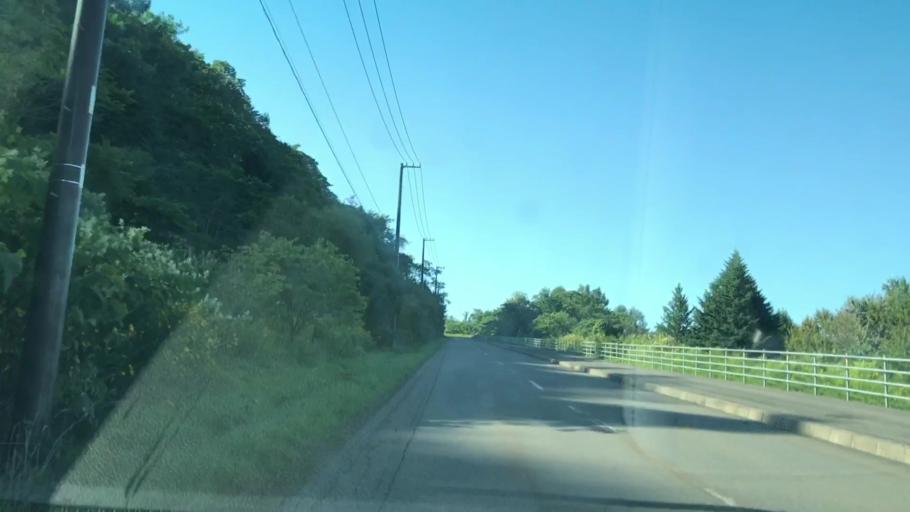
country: JP
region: Hokkaido
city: Date
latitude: 42.5637
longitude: 140.8076
